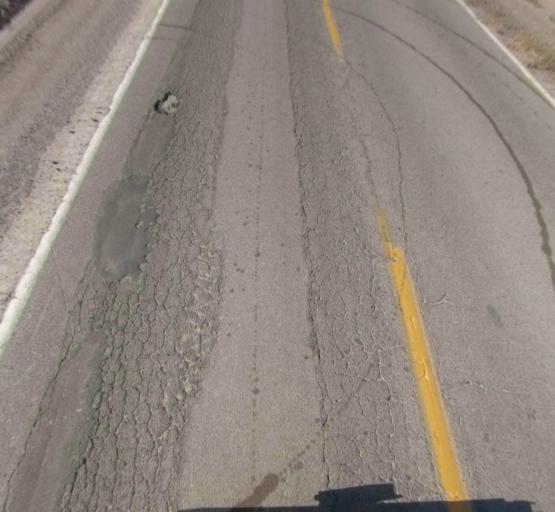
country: US
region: California
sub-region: Madera County
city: Fairmead
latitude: 36.9409
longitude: -120.2559
